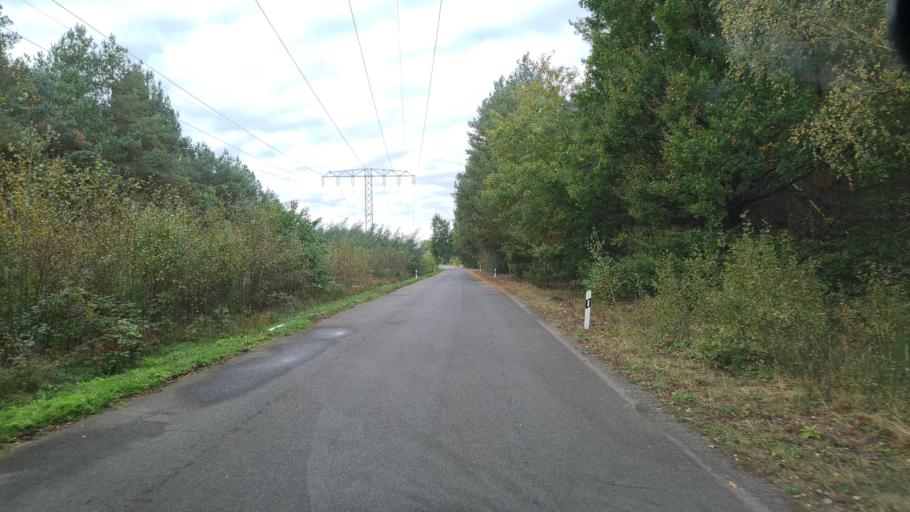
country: DE
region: Brandenburg
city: Altdobern
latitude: 51.6738
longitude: 14.0946
